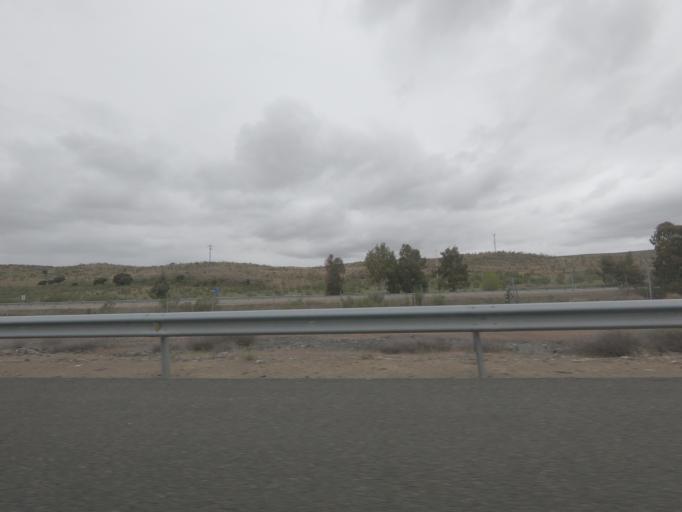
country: ES
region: Extremadura
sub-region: Provincia de Caceres
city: Mirabel
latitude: 39.9139
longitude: -6.2471
